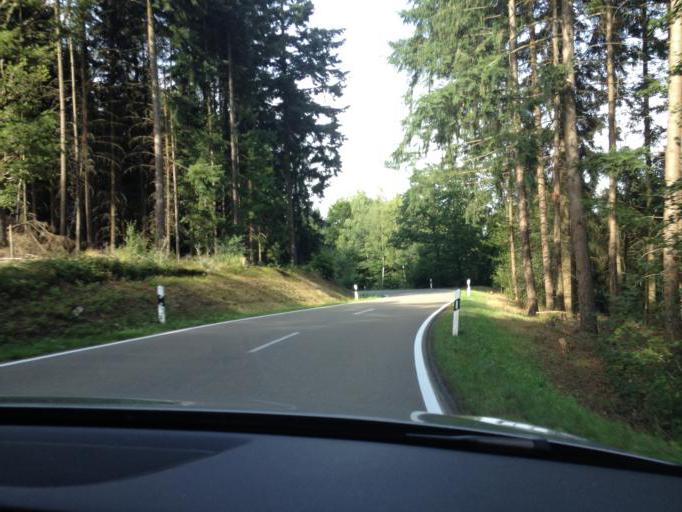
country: DE
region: Rheinland-Pfalz
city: Dunzweiler
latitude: 49.4070
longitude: 7.2980
